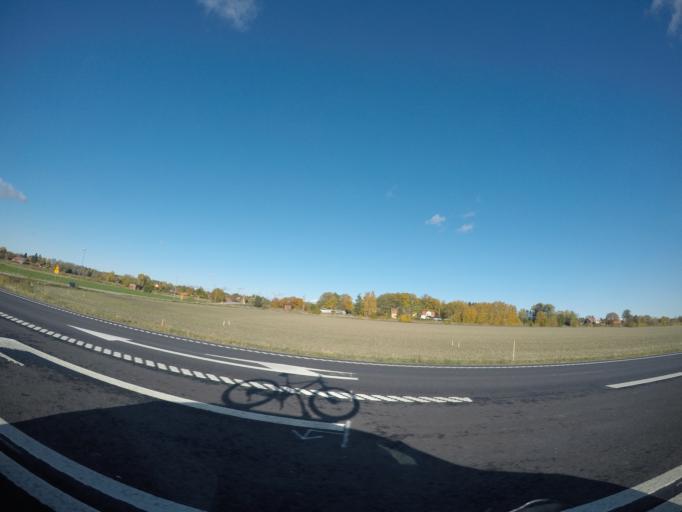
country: SE
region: Vaestmanland
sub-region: Kungsors Kommun
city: Kungsoer
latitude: 59.4144
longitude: 16.1950
